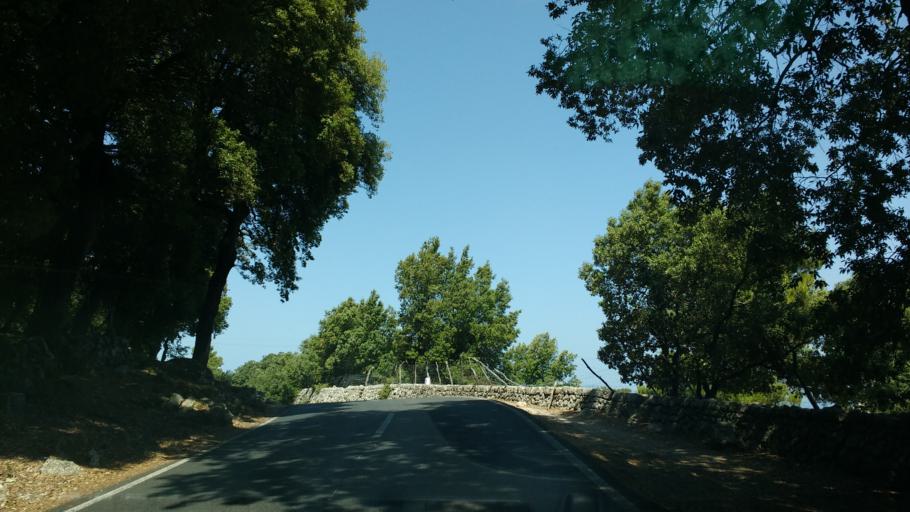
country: ES
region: Balearic Islands
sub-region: Illes Balears
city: Escorca
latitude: 39.8247
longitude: 2.8505
